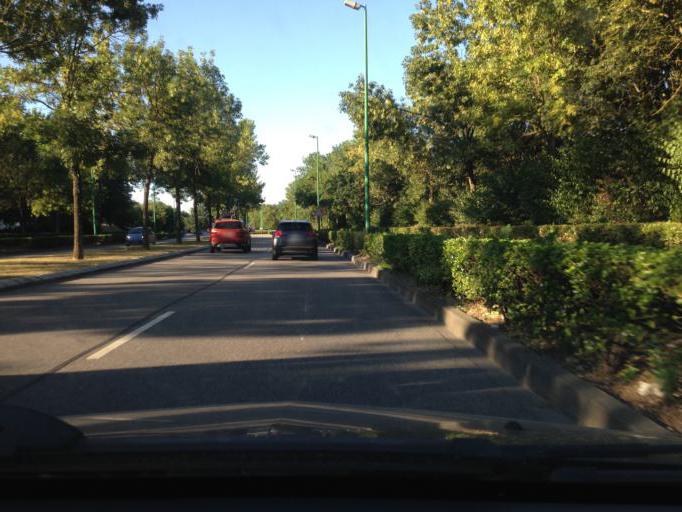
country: FR
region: Ile-de-France
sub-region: Departement des Yvelines
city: Voisins-le-Bretonneux
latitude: 48.7656
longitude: 2.0529
